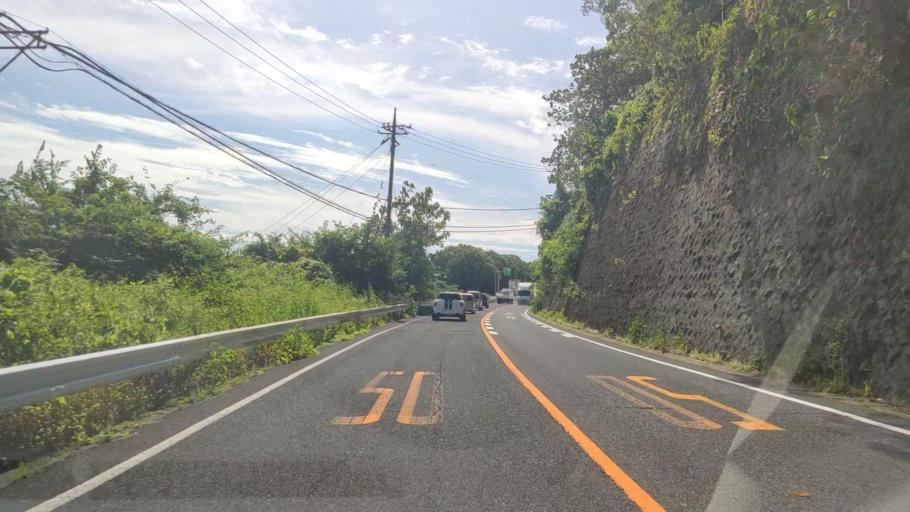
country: JP
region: Gunma
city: Numata
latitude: 36.5642
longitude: 139.0377
